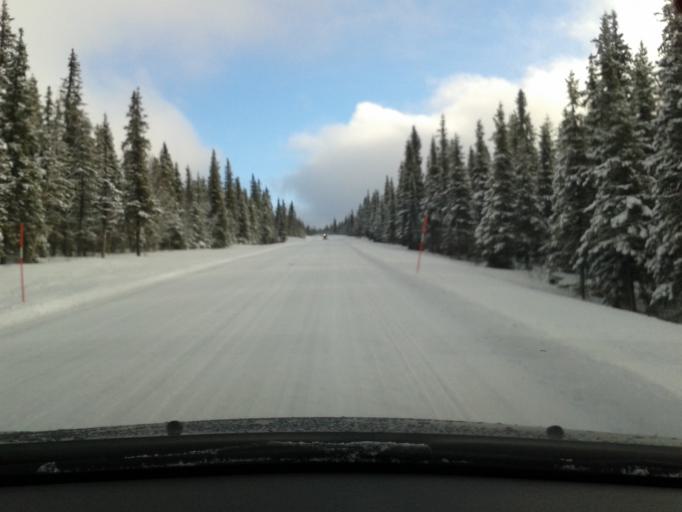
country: SE
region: Vaesterbotten
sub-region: Vilhelmina Kommun
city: Sjoberg
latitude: 65.2511
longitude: 15.6259
